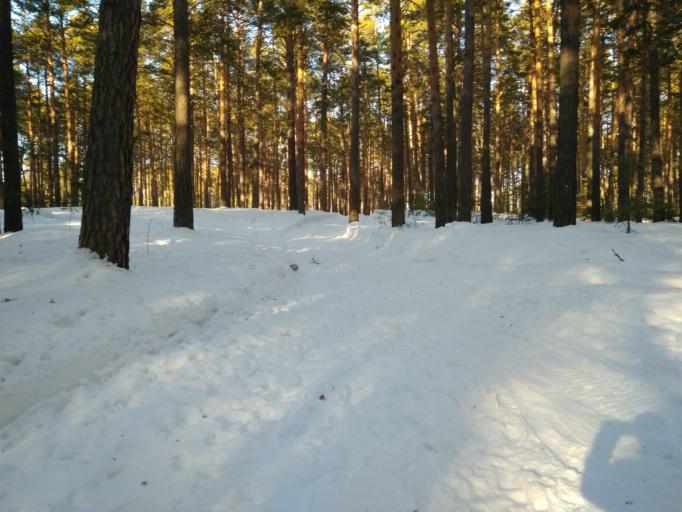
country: RU
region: Tomsk
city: Timiryazevskoye
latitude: 56.4839
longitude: 84.8750
